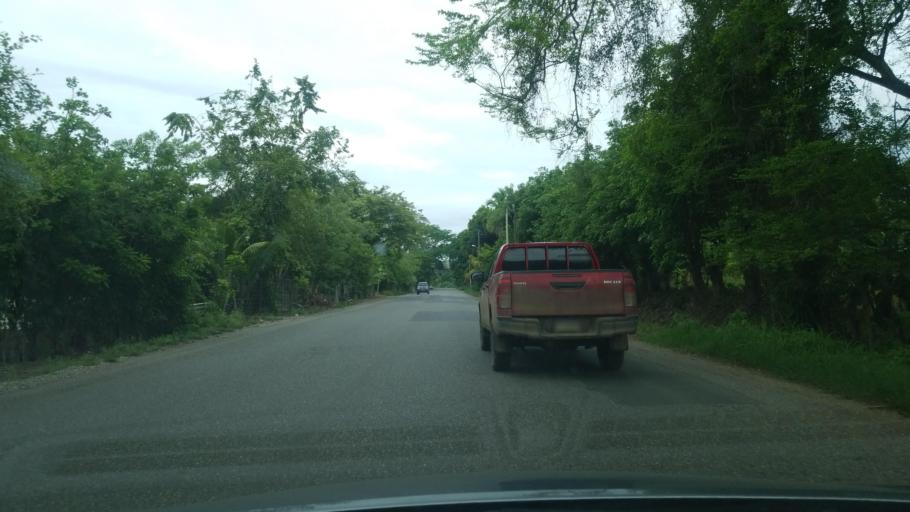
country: HN
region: Santa Barbara
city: La Flecha
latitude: 15.2996
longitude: -88.4745
